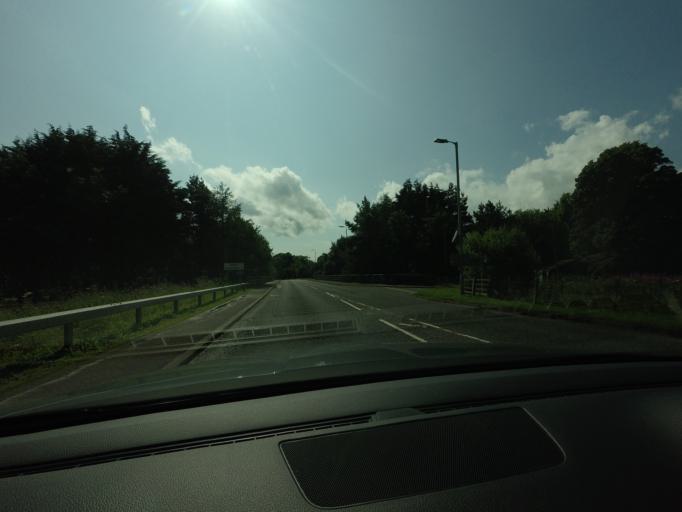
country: GB
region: Scotland
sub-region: Highland
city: Alness
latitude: 57.6908
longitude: -4.2417
